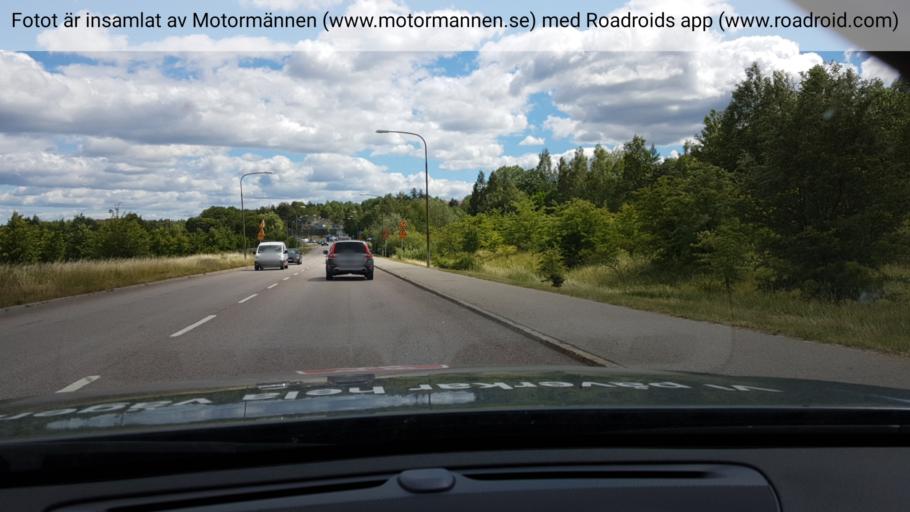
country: SE
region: Stockholm
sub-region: Stockholms Kommun
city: Arsta
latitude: 59.2881
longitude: 18.0415
